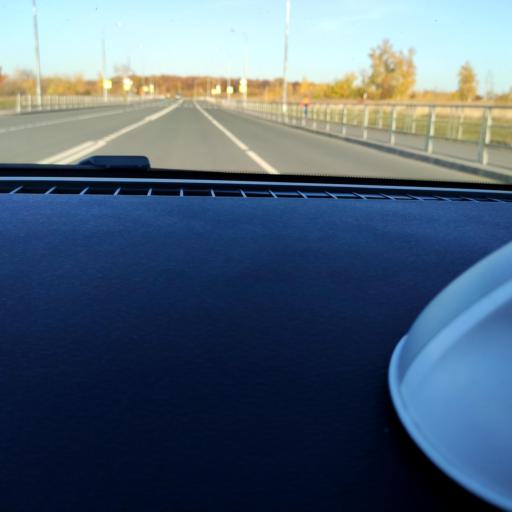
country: RU
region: Samara
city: Samara
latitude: 53.2904
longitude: 50.2357
